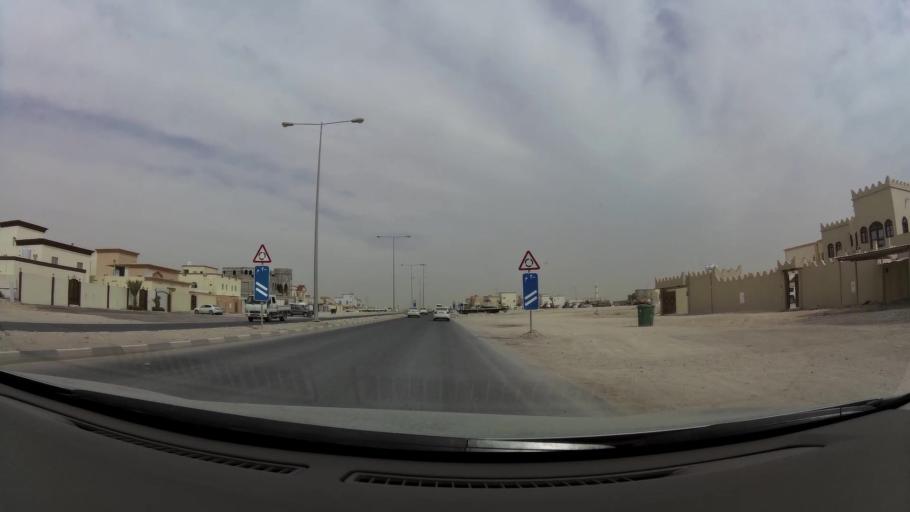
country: QA
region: Baladiyat ad Dawhah
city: Doha
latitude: 25.2108
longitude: 51.4829
